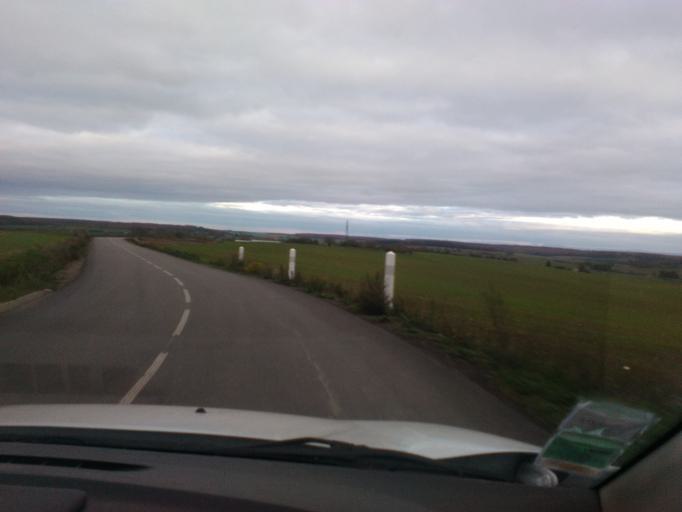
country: FR
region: Lorraine
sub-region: Departement des Vosges
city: Darnieulles
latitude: 48.2346
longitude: 6.3246
